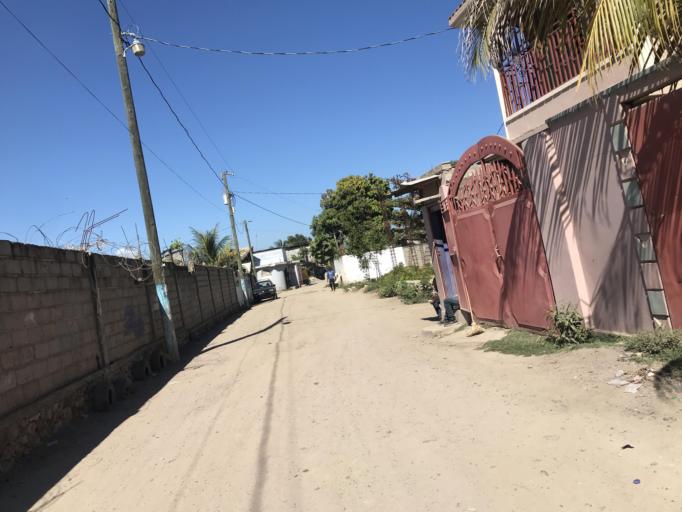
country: HT
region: Nord
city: Limonade
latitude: 19.6699
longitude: -72.1279
